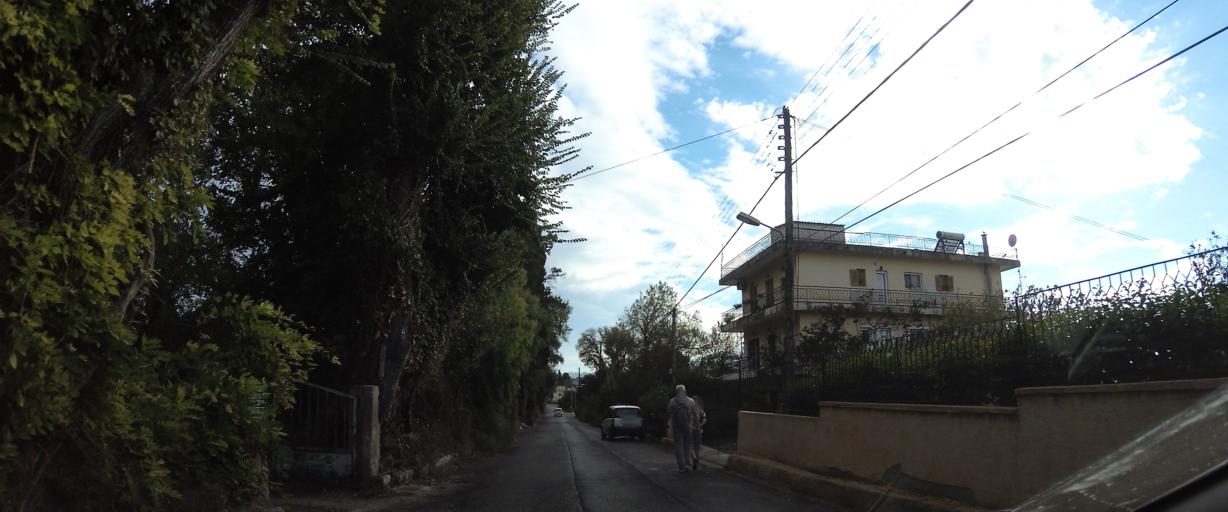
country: GR
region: Ionian Islands
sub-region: Nomos Kerkyras
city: Kerkyra
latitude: 39.6035
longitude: 19.9204
